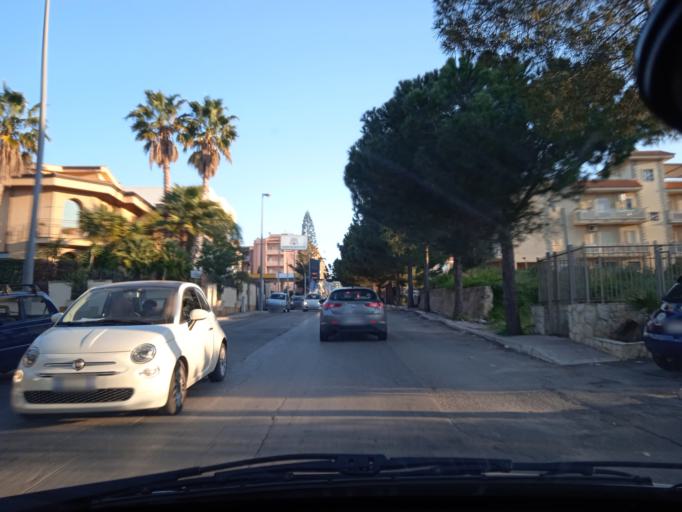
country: IT
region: Sicily
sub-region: Palermo
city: Bagheria
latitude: 38.0859
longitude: 13.5010
